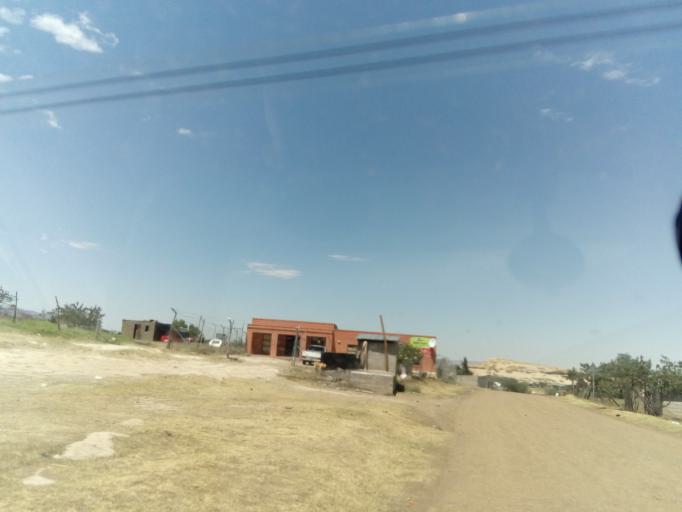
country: LS
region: Berea
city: Teyateyaneng
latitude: -29.1397
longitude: 27.8767
